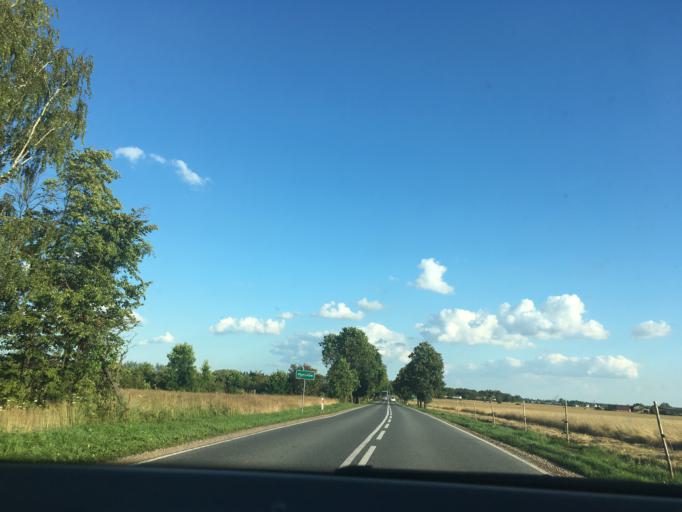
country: PL
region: Masovian Voivodeship
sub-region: Powiat losicki
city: Sarnaki
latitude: 52.2950
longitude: 22.8233
